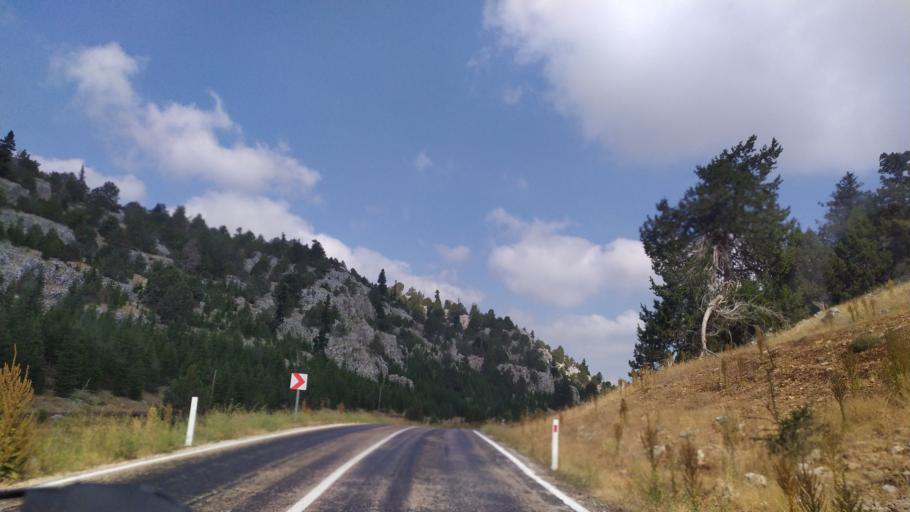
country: TR
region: Mersin
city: Kirobasi
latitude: 36.6157
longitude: 33.8763
